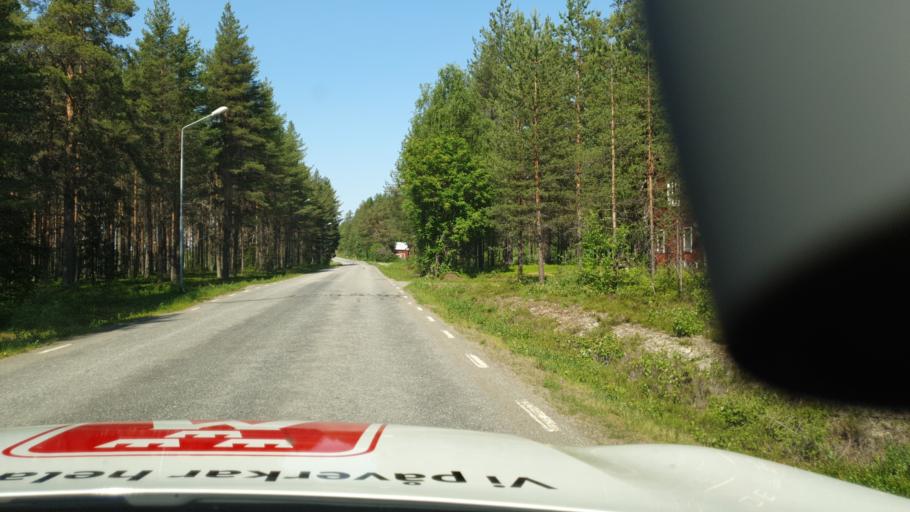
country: SE
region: Vaesterbotten
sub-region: Skelleftea Kommun
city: Langsele
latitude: 64.9555
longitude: 19.9139
